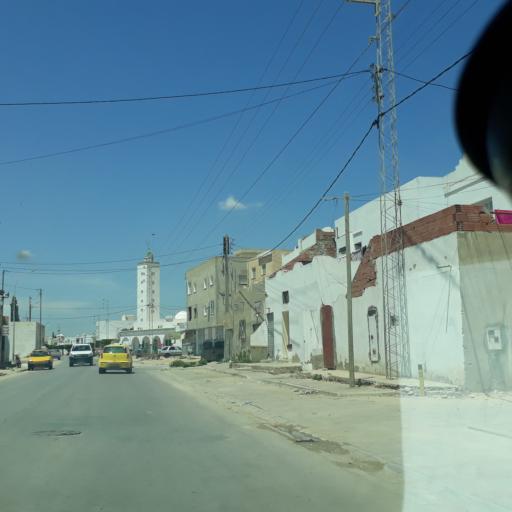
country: TN
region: Safaqis
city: Al Qarmadah
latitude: 34.8119
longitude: 10.7481
